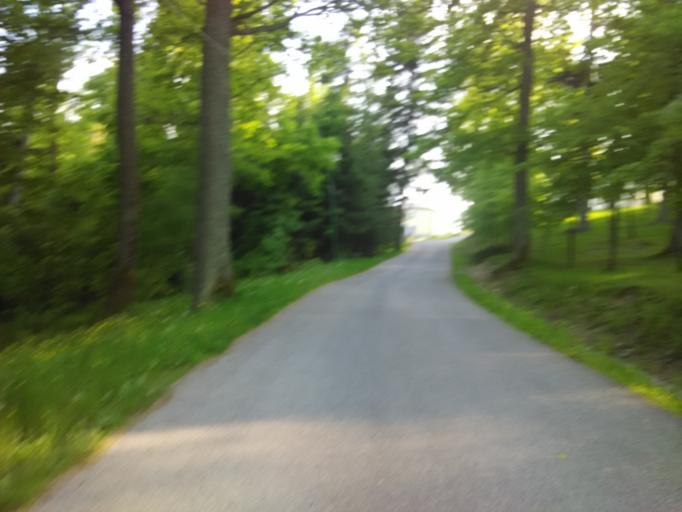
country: SK
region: Presovsky
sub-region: Okres Presov
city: Levoca
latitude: 49.0443
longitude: 20.5995
